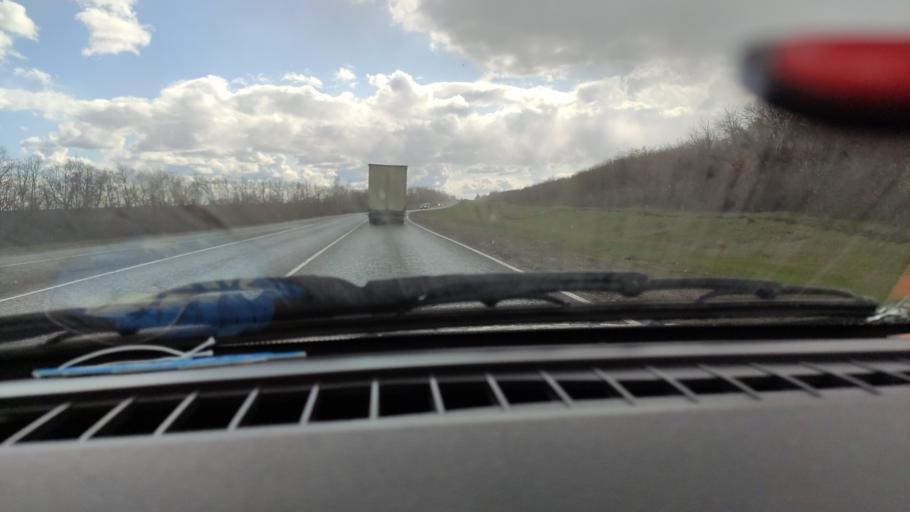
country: RU
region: Saratov
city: Balakovo
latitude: 52.1047
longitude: 47.7411
